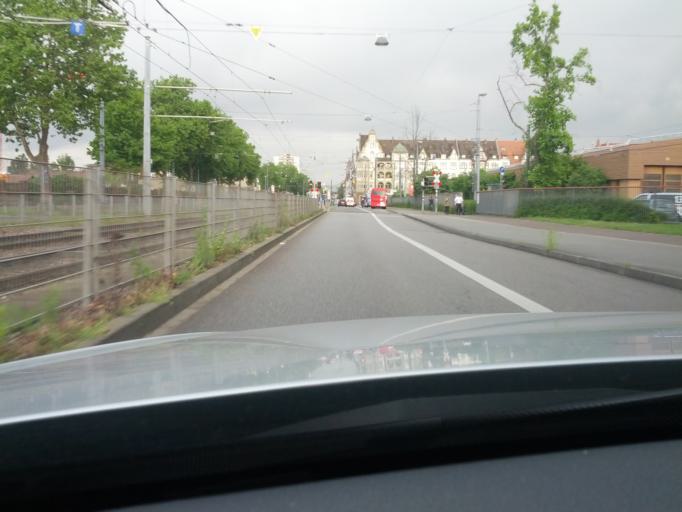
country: DE
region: Baden-Wuerttemberg
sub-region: Karlsruhe Region
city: Karlsruhe
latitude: 49.0059
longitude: 8.4340
